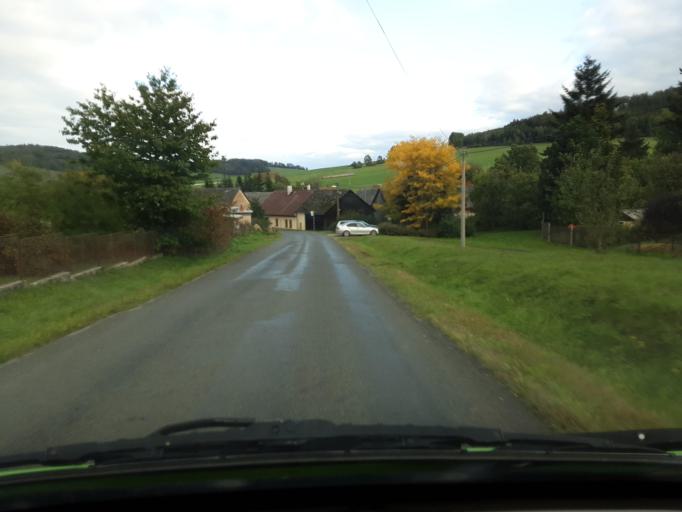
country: CZ
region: Plzensky
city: Janovice nad Uhlavou
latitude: 49.3862
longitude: 13.1458
